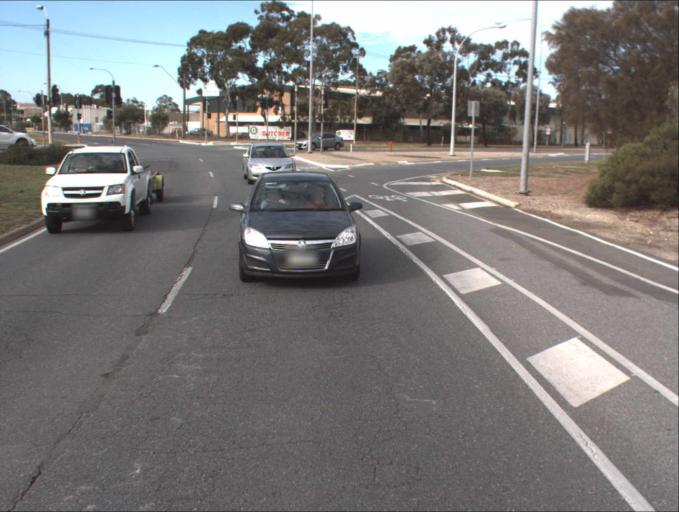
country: AU
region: South Australia
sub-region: Charles Sturt
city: West Lakes Shore
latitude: -34.8591
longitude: 138.5027
